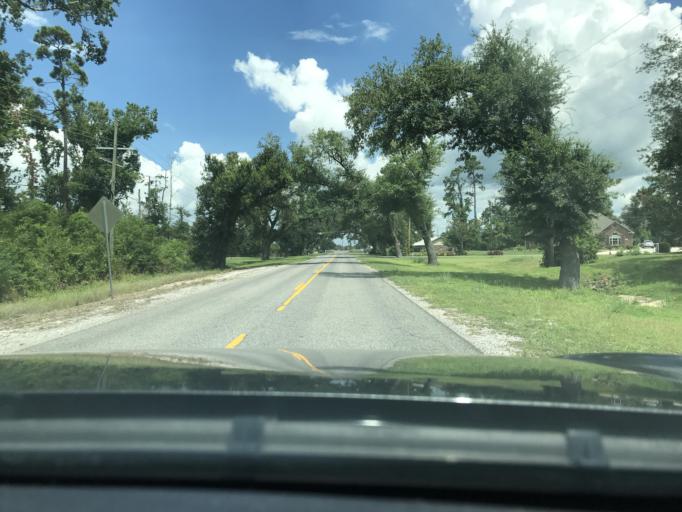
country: US
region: Louisiana
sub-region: Calcasieu Parish
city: Moss Bluff
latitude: 30.3058
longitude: -93.1922
